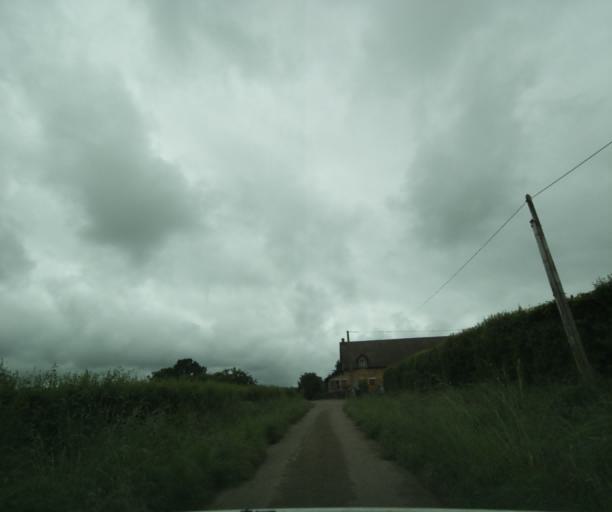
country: FR
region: Bourgogne
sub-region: Departement de Saone-et-Loire
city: Charolles
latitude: 46.4884
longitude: 4.3214
